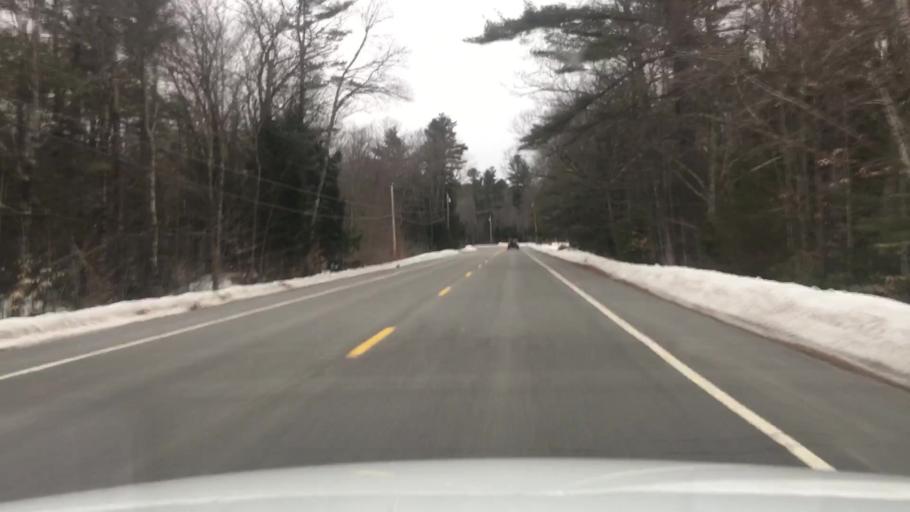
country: US
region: Maine
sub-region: York County
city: Limerick
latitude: 43.7231
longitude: -70.8135
